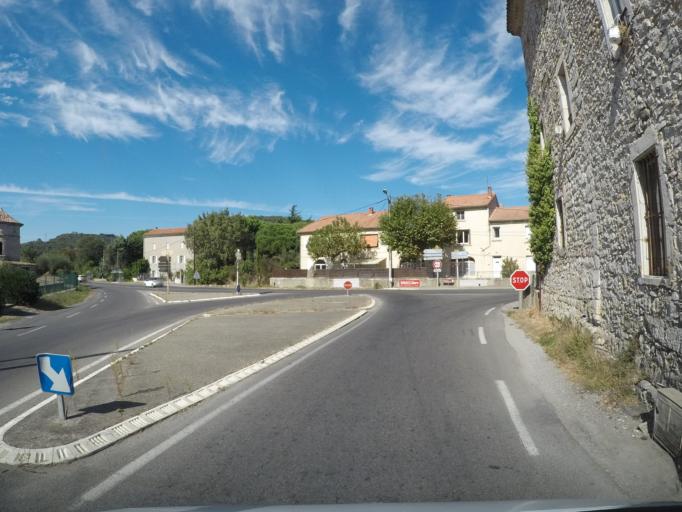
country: FR
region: Languedoc-Roussillon
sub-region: Departement du Gard
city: Boisset-et-Gaujac
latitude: 44.0356
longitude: 4.0033
